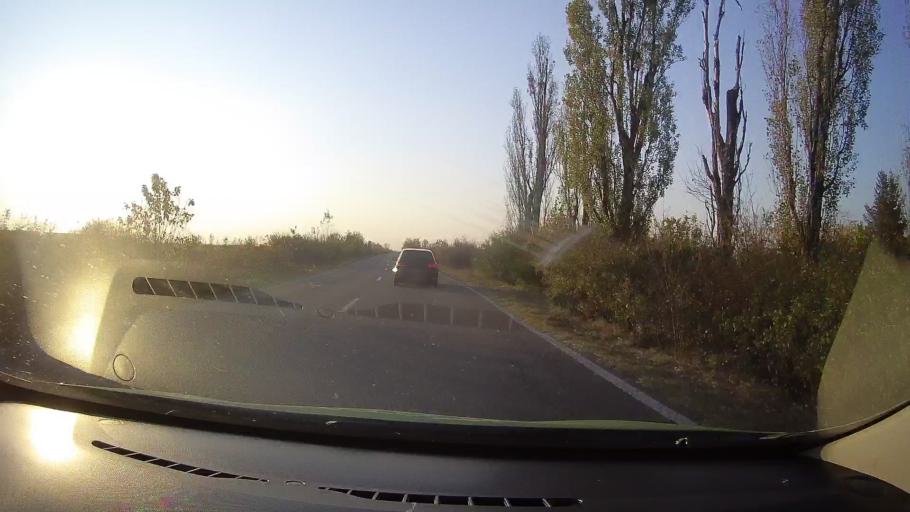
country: RO
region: Arad
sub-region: Comuna Barsa
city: Barsa
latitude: 46.4034
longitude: 22.0281
